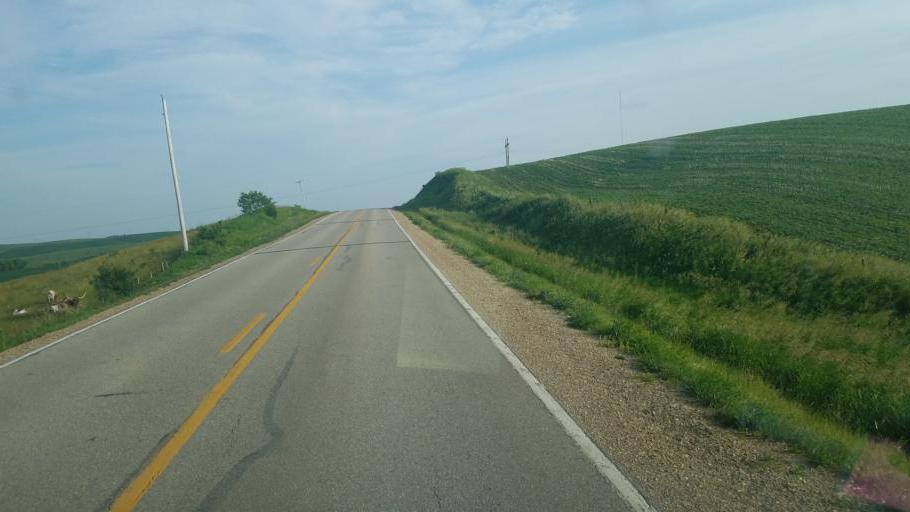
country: US
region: Iowa
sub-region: Tama County
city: Tama
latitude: 41.9587
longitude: -92.7082
